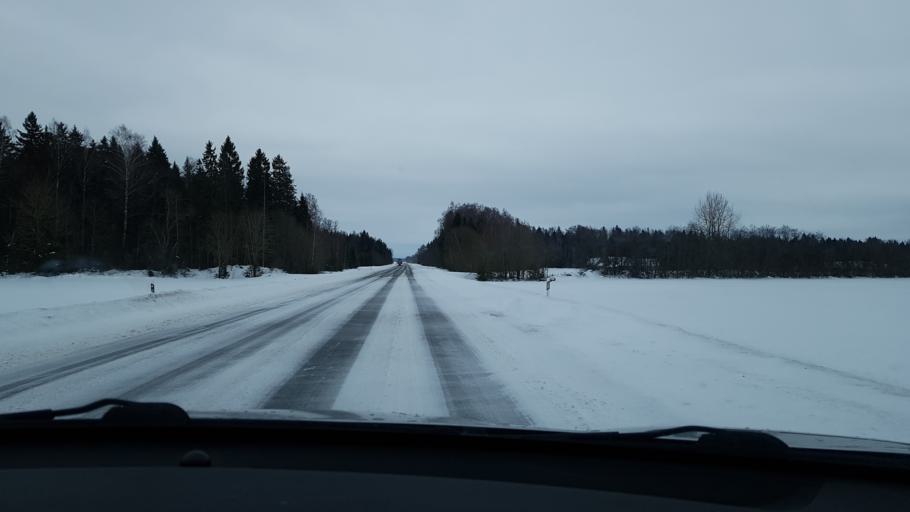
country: EE
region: Jaervamaa
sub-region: Jaerva-Jaani vald
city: Jarva-Jaani
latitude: 59.1362
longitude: 25.7737
